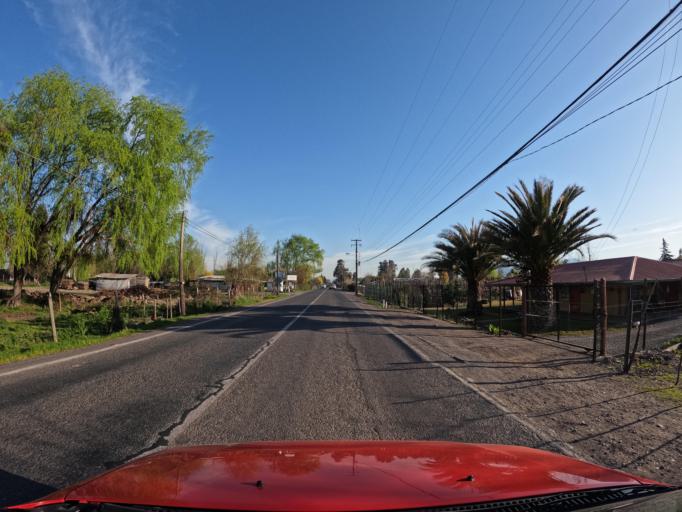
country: CL
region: Maule
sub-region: Provincia de Curico
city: Rauco
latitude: -34.8691
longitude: -71.2648
